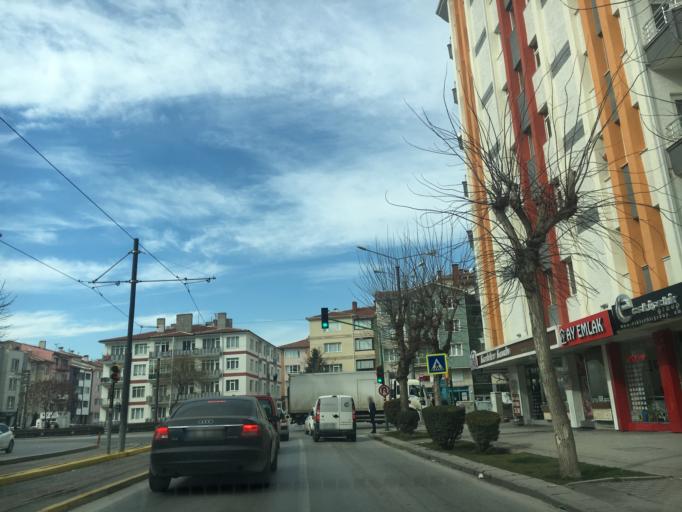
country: TR
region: Eskisehir
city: Eskisehir
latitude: 39.7674
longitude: 30.5017
